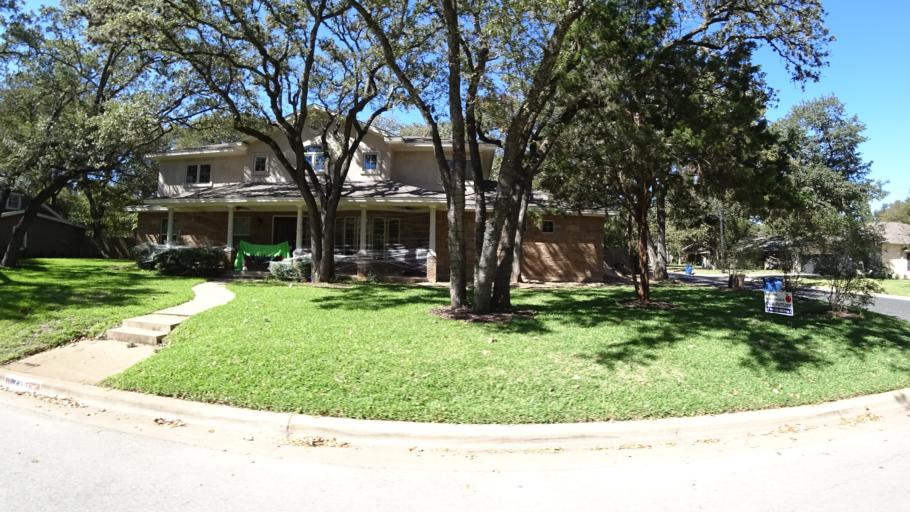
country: US
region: Texas
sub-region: Travis County
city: West Lake Hills
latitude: 30.3633
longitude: -97.7669
